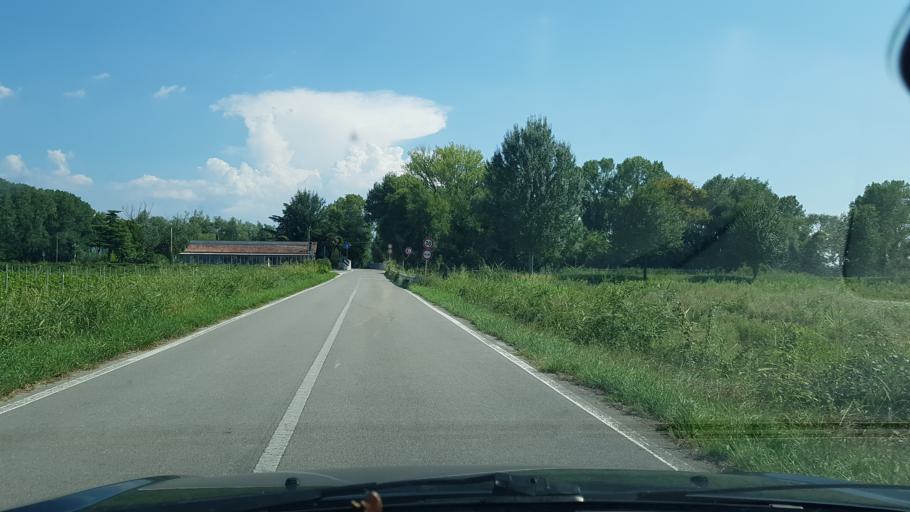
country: IT
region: Friuli Venezia Giulia
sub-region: Provincia di Gorizia
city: Staranzano
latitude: 45.7805
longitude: 13.5099
